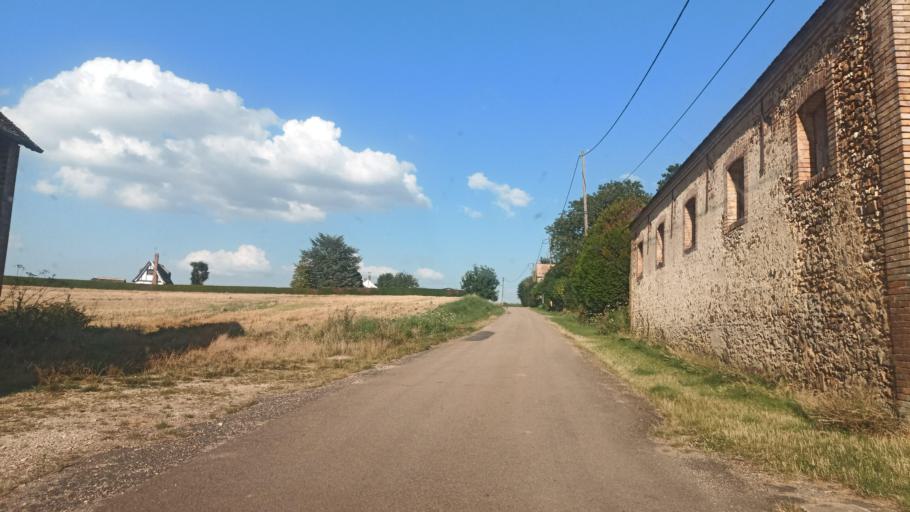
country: FR
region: Bourgogne
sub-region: Departement de l'Yonne
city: Saint-Valerien
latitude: 48.2277
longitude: 3.0714
